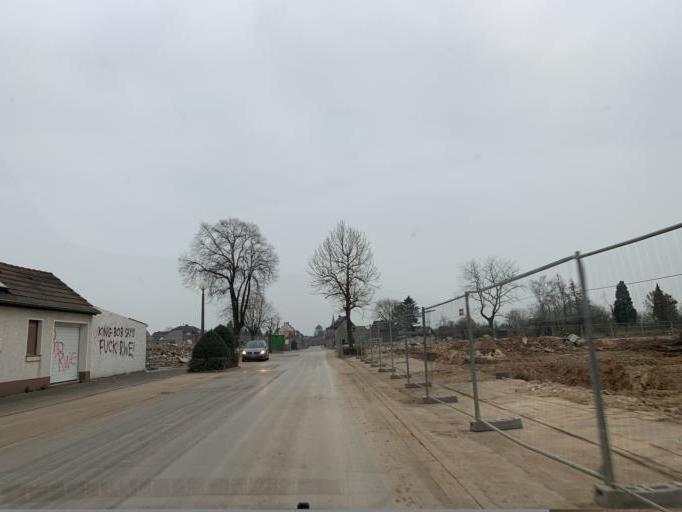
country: DE
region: North Rhine-Westphalia
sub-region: Regierungsbezirk Koln
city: Elsdorf
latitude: 50.8841
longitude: 6.5928
